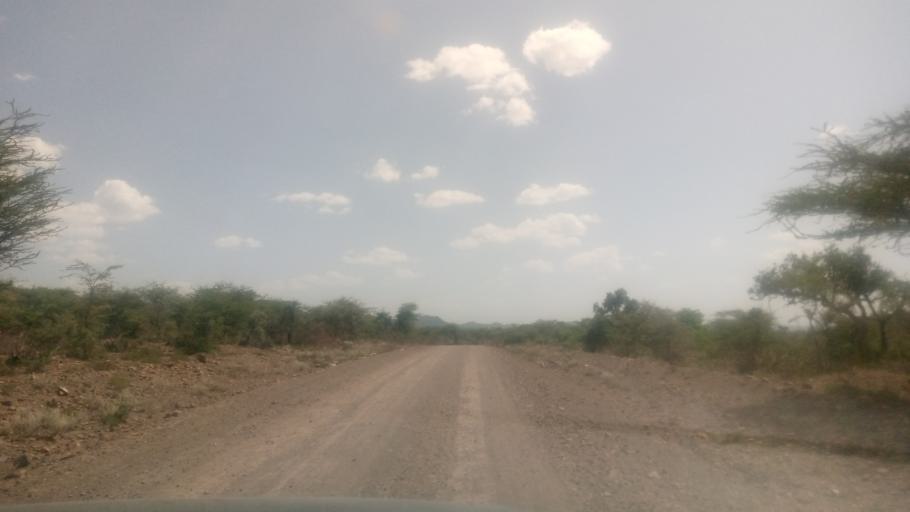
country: ET
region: Oromiya
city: Deder
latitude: 9.5096
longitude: 41.3156
